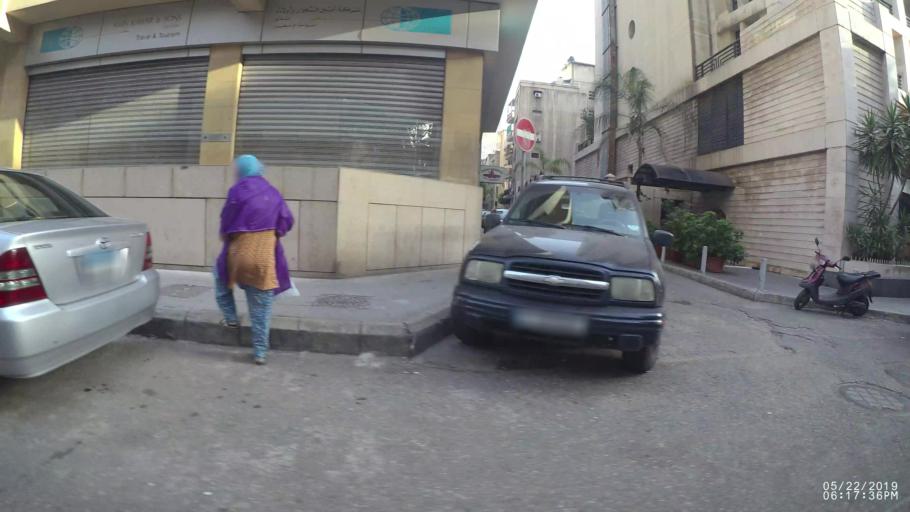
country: LB
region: Beyrouth
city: Ra's Bayrut
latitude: 33.8948
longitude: 35.4804
